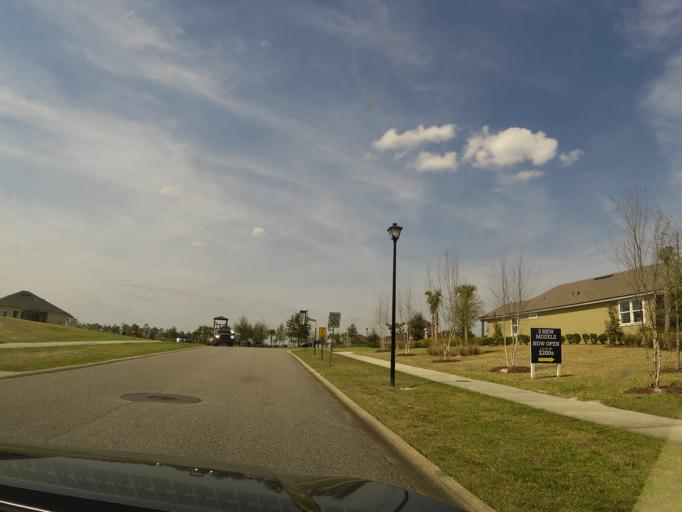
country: US
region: Florida
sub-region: Clay County
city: Middleburg
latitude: 30.0978
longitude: -81.8553
